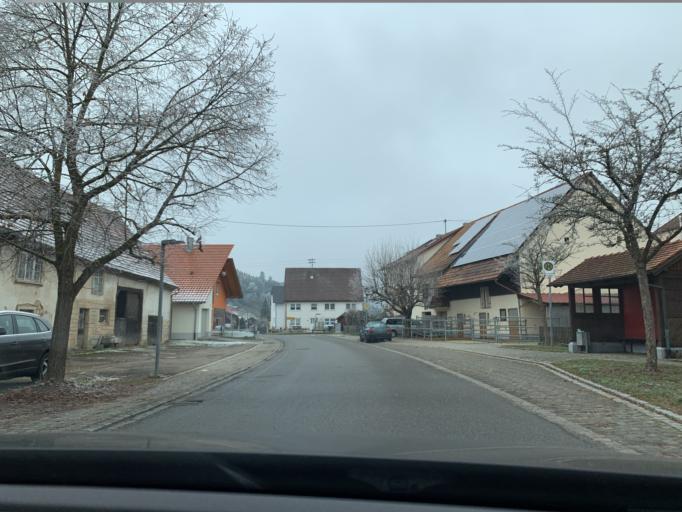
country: DE
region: Baden-Wuerttemberg
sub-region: Freiburg Region
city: Tengen
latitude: 47.8643
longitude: 8.6693
